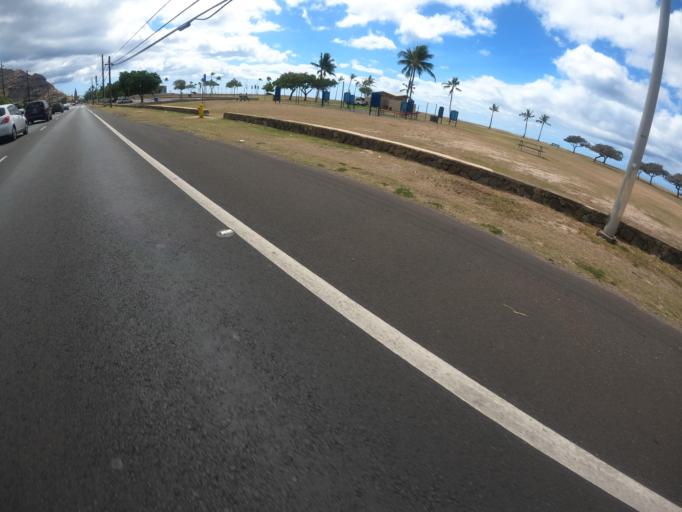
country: US
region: Hawaii
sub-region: Honolulu County
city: Ma'ili
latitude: 21.4181
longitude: -158.1773
